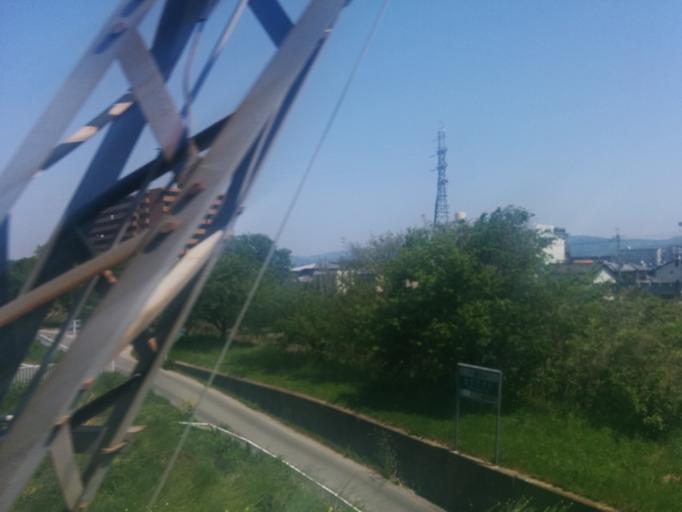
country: JP
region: Nara
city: Kashihara-shi
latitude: 34.5157
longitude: 135.7871
